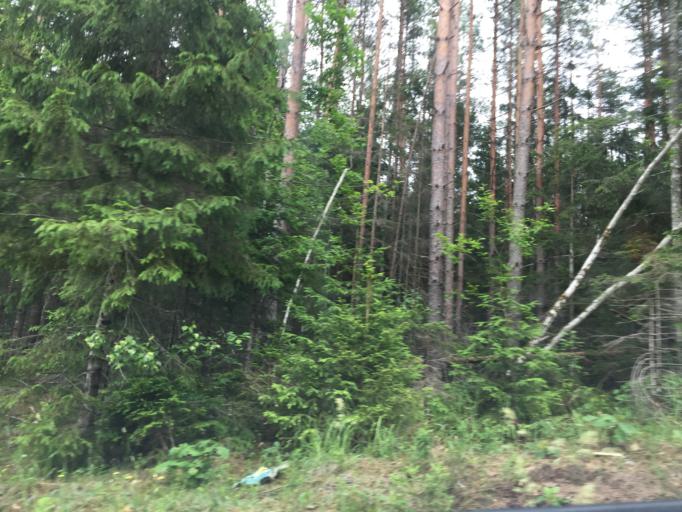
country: LV
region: Tukuma Rajons
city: Tukums
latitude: 57.0158
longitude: 23.0873
